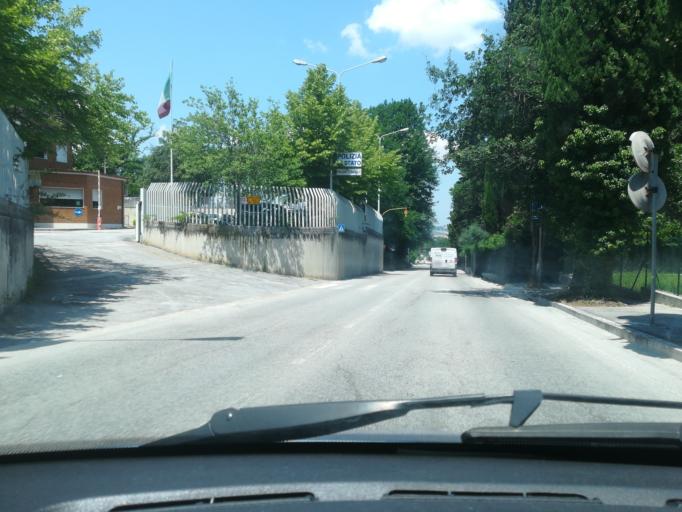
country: IT
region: The Marches
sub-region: Provincia di Macerata
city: Villa Potenza
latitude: 43.3112
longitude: 13.4354
